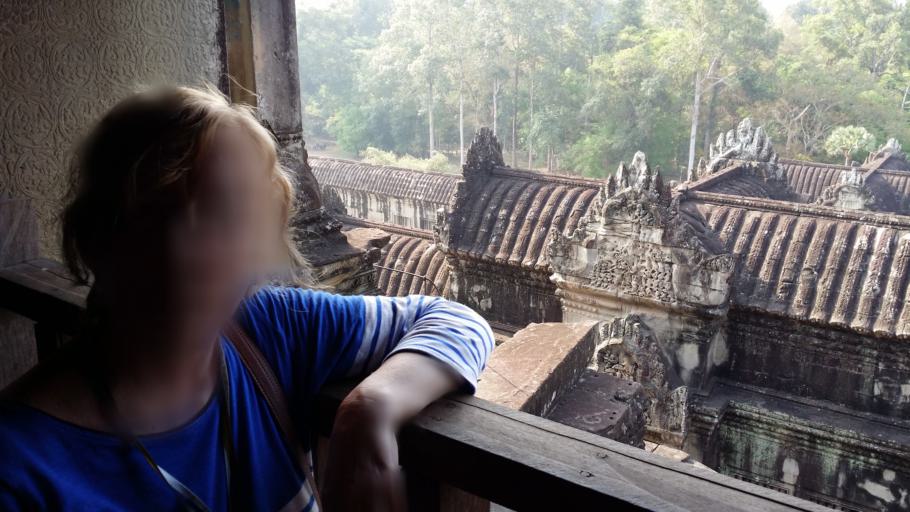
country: KH
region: Siem Reap
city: Siem Reap
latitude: 13.4122
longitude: 103.8667
